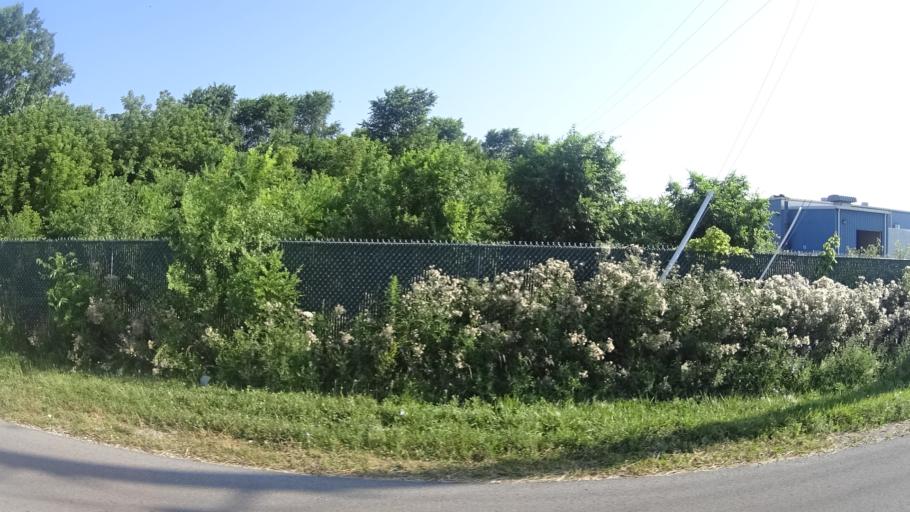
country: US
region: Ohio
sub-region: Erie County
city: Sandusky
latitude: 41.4497
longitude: -82.6853
